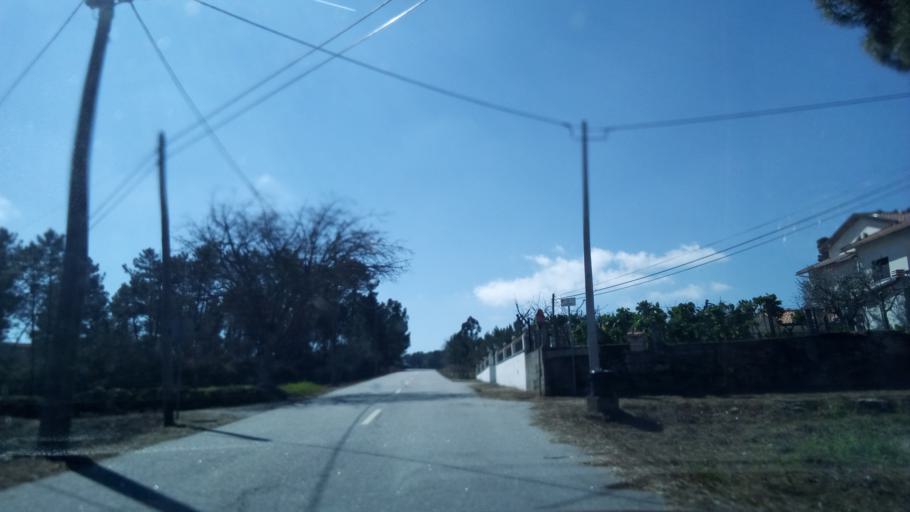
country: PT
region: Guarda
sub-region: Fornos de Algodres
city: Fornos de Algodres
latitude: 40.6457
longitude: -7.5318
